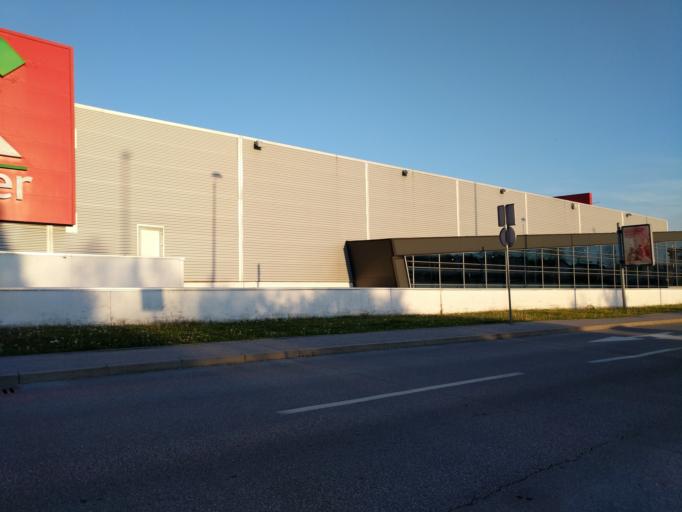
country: HR
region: Grad Zagreb
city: Dubrava
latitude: 45.8287
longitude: 16.0791
